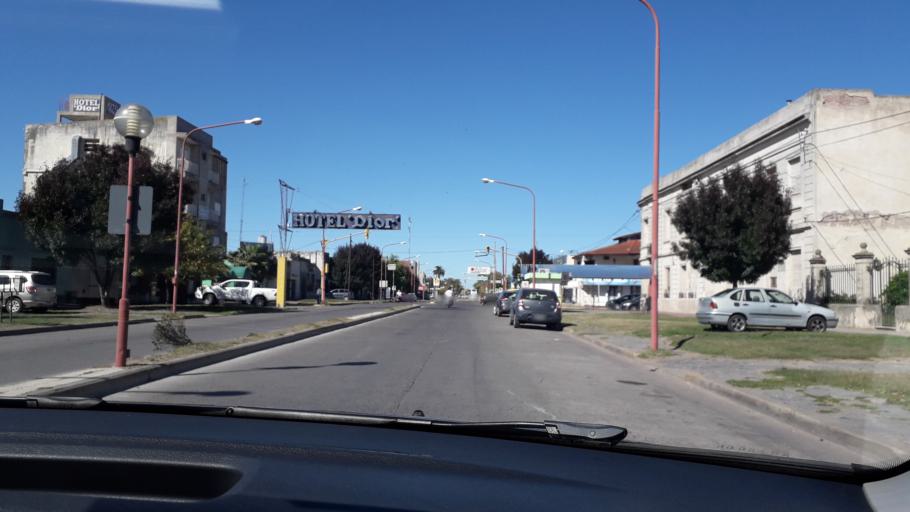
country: AR
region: Buenos Aires
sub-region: Partido de Azul
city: Azul
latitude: -36.7819
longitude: -59.8534
